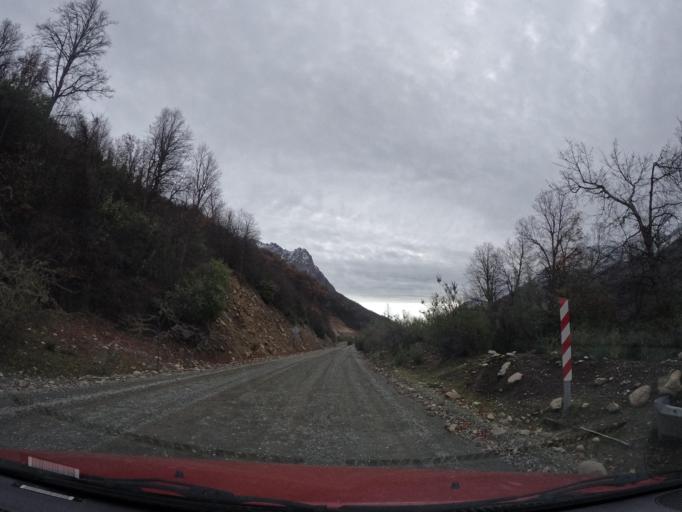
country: CL
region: Maule
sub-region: Provincia de Linares
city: Colbun
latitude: -35.8584
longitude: -71.1403
